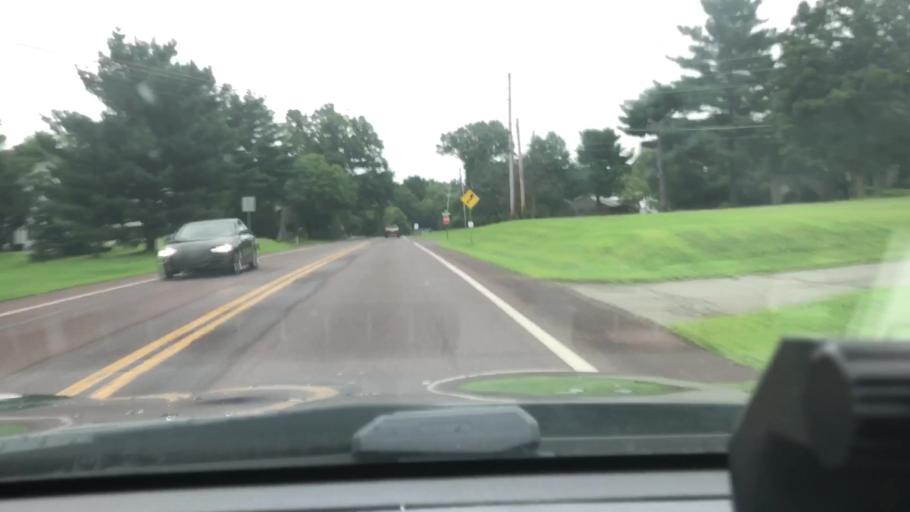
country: US
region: Pennsylvania
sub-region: Montgomery County
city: Gilbertsville
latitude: 40.3160
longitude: -75.5889
